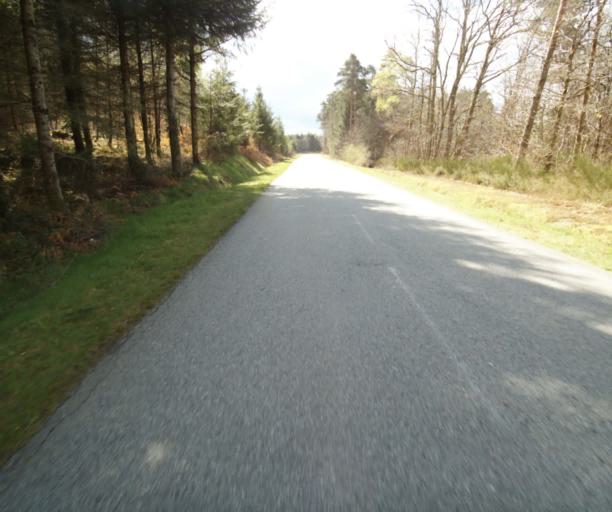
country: FR
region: Limousin
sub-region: Departement de la Correze
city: Correze
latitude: 45.2951
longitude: 1.8956
